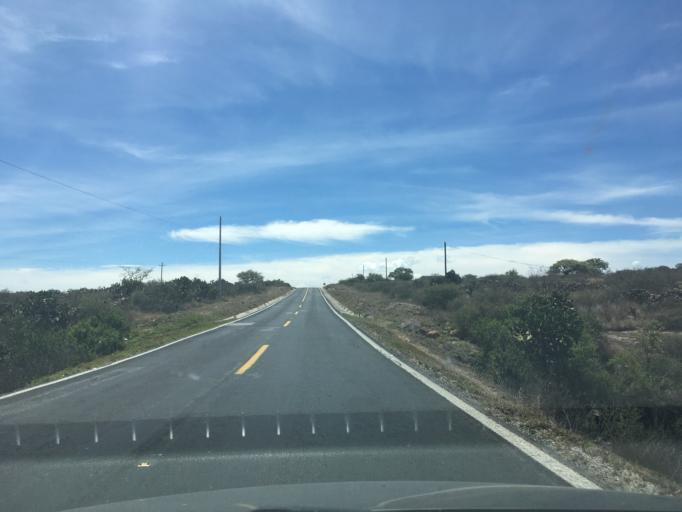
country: MX
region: Hidalgo
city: Huichapan
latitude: 20.4279
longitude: -99.5184
